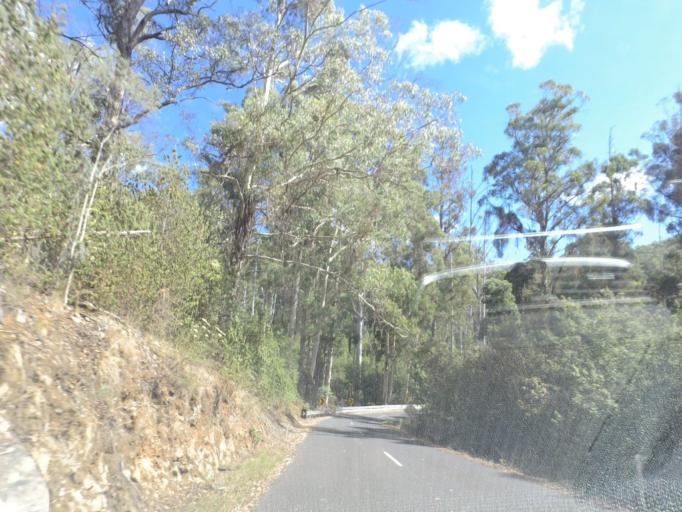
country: AU
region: Victoria
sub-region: Murrindindi
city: Alexandra
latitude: -37.3275
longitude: 145.9332
